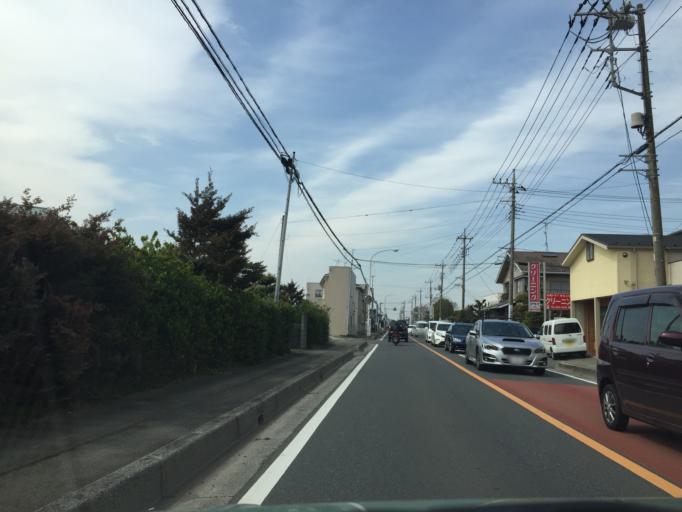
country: JP
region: Saitama
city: Yono
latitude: 35.8868
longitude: 139.5905
